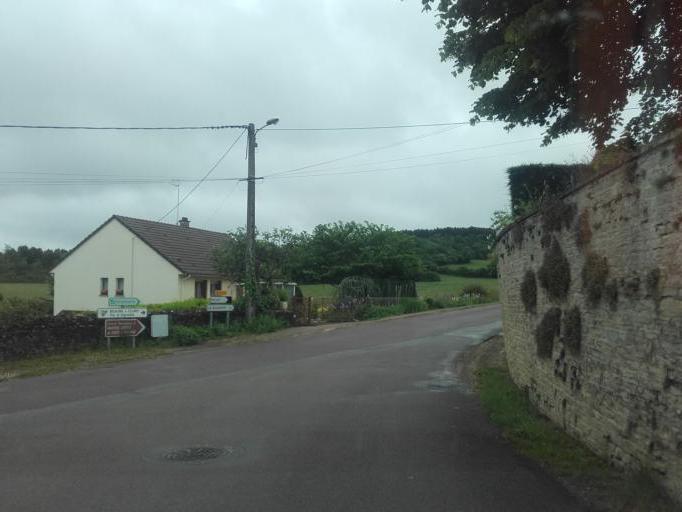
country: FR
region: Bourgogne
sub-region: Departement de la Cote-d'Or
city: Nolay
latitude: 46.9692
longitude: 4.6837
